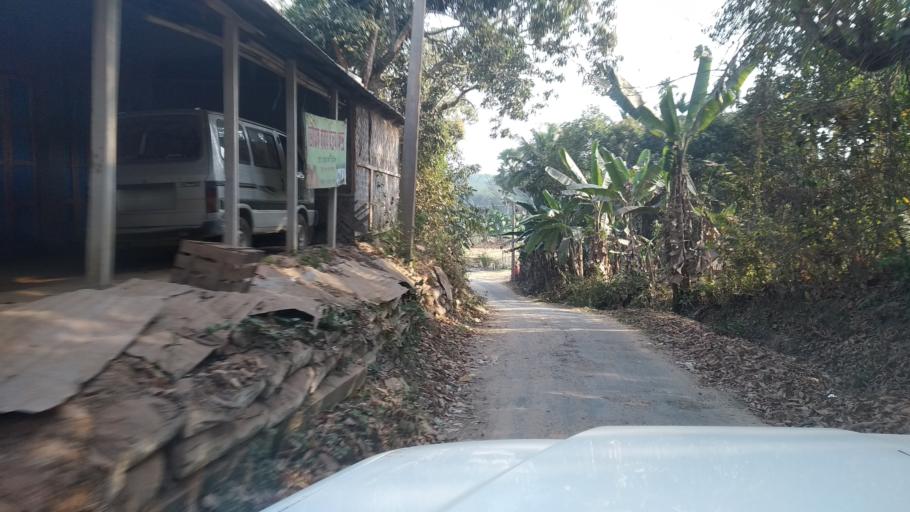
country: IN
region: Tripura
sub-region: West Tripura
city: Sonamura
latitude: 23.4316
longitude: 91.3119
